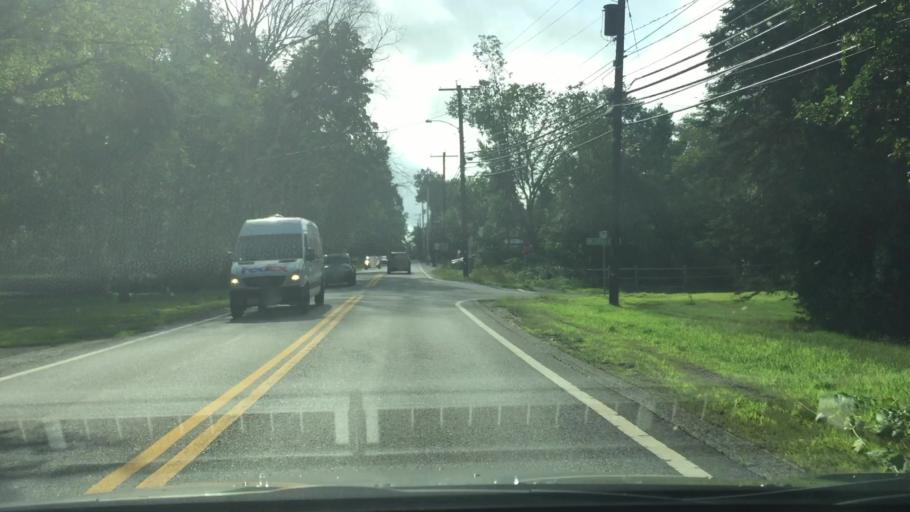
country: US
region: Massachusetts
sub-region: Middlesex County
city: Stow
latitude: 42.4770
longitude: -71.4811
